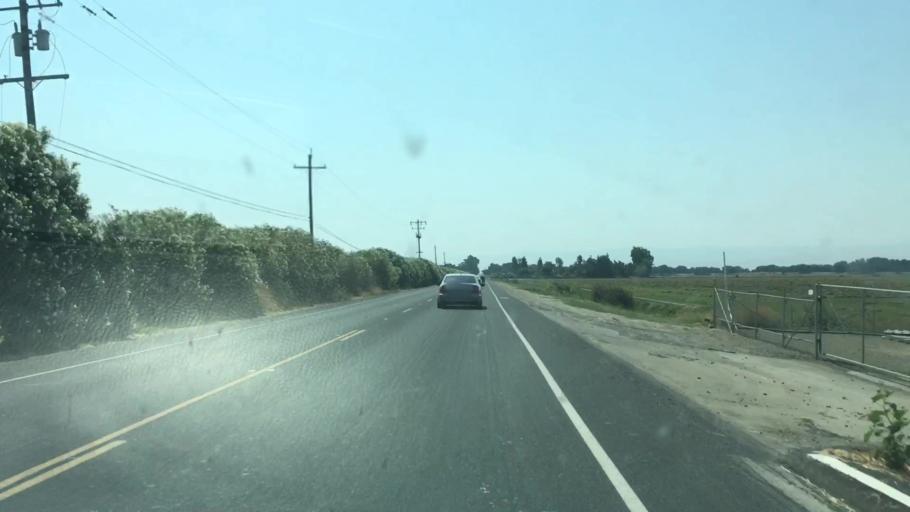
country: US
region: California
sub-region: San Joaquin County
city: Tracy
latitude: 37.8168
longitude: -121.4497
